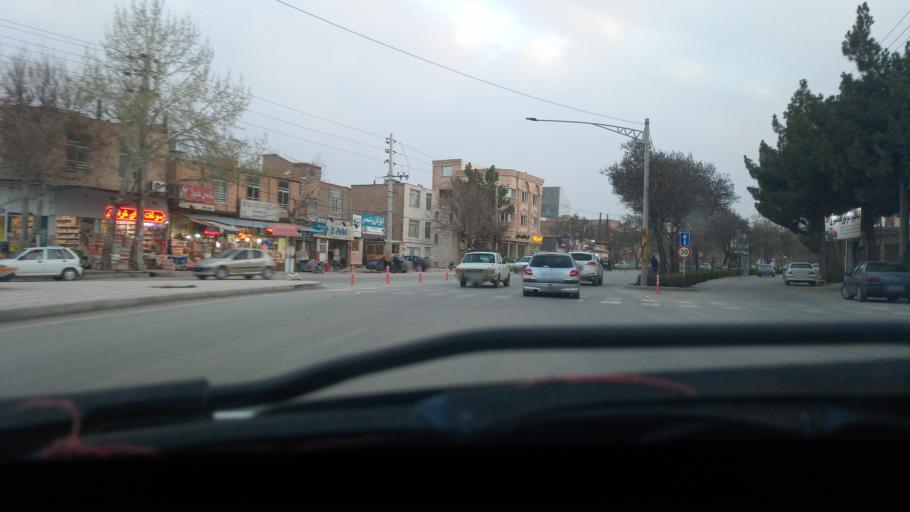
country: IR
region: Khorasan-e Shomali
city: Bojnurd
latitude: 37.4658
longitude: 57.3438
